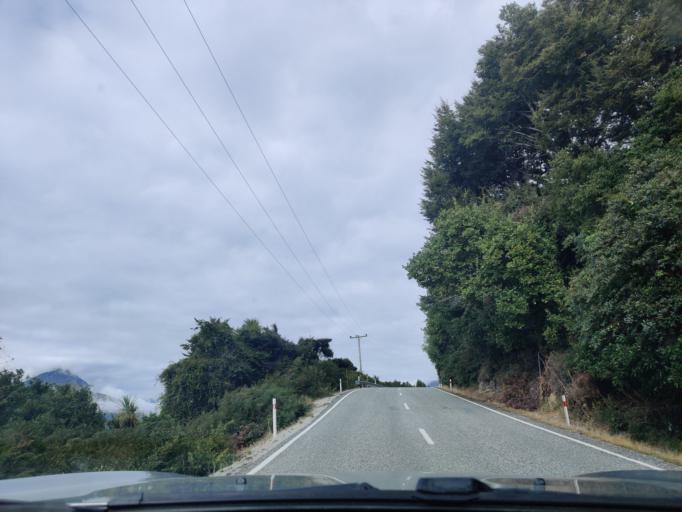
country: NZ
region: Otago
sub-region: Queenstown-Lakes District
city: Queenstown
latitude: -45.0743
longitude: 168.4953
